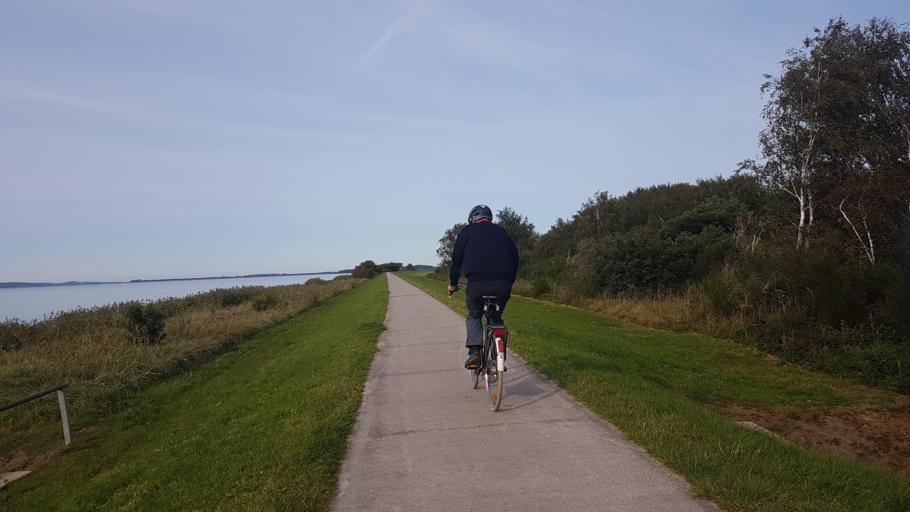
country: DE
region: Mecklenburg-Vorpommern
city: Hiddensee
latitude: 54.4713
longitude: 13.1402
